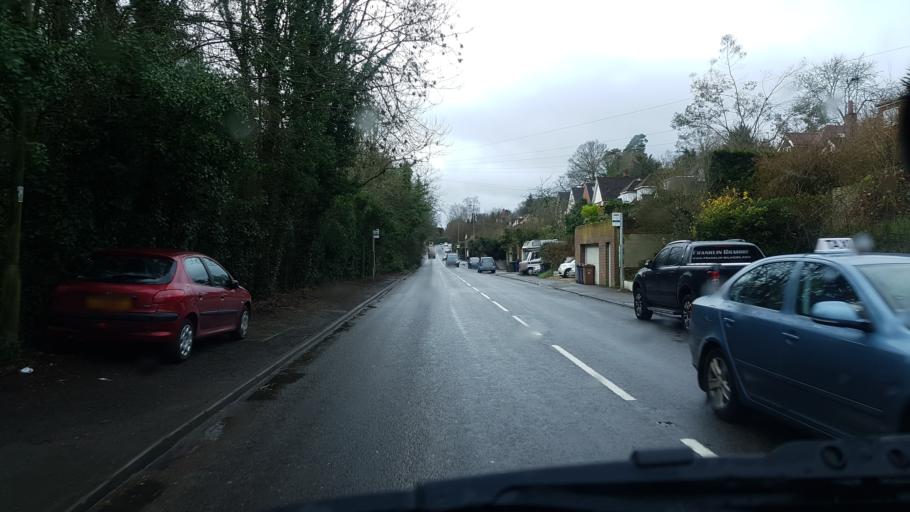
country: GB
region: England
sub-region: Surrey
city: Godalming
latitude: 51.1764
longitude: -0.6278
